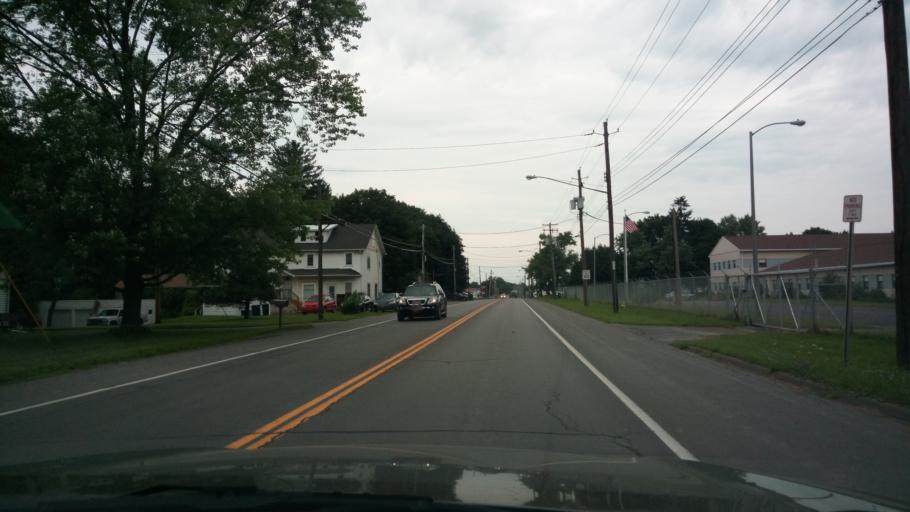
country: US
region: New York
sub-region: Chemung County
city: Elmira Heights
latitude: 42.1398
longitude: -76.8137
